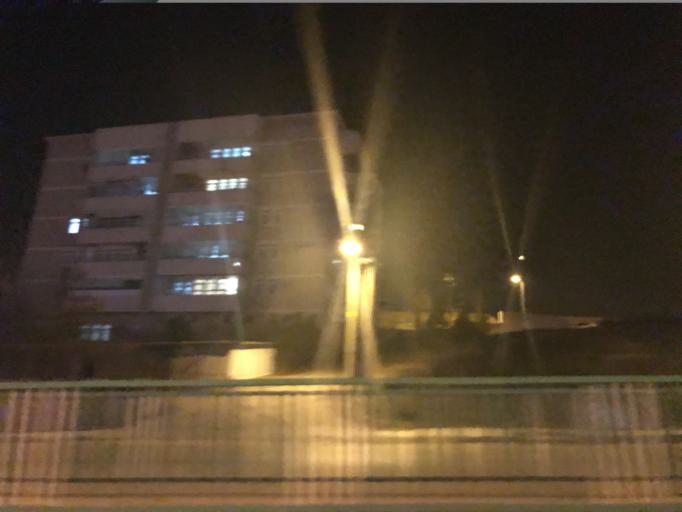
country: TR
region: Karabuk
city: Karabuk
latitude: 41.2221
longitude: 32.6623
